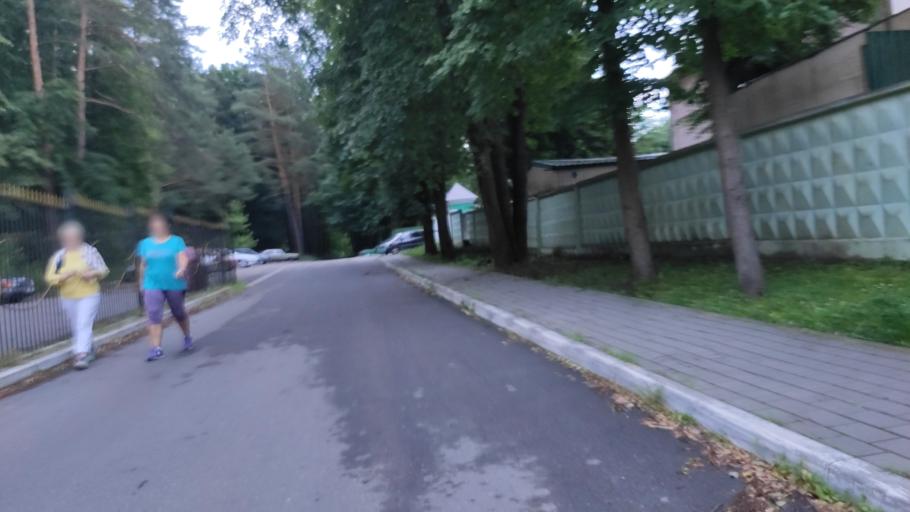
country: BY
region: Minsk
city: Zhdanovichy
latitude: 53.9679
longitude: 27.4319
